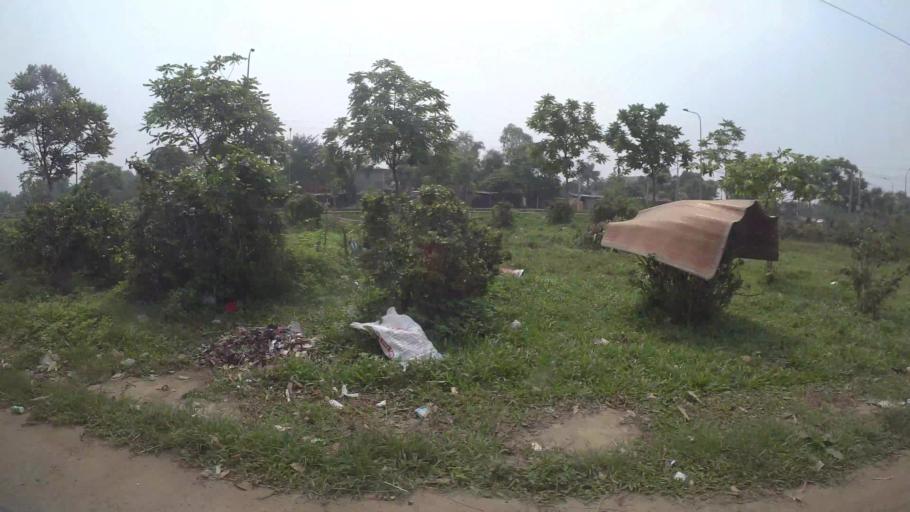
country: VN
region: Ha Noi
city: Lien Quan
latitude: 20.9880
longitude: 105.5358
